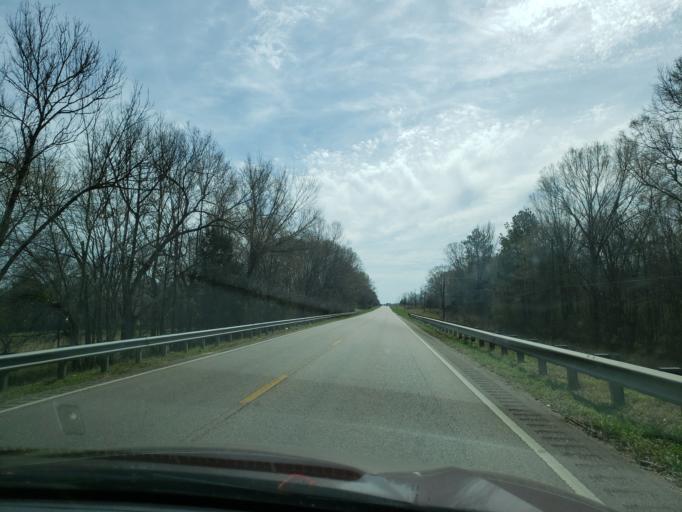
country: US
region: Alabama
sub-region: Dallas County
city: Selma
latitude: 32.4490
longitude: -87.0761
